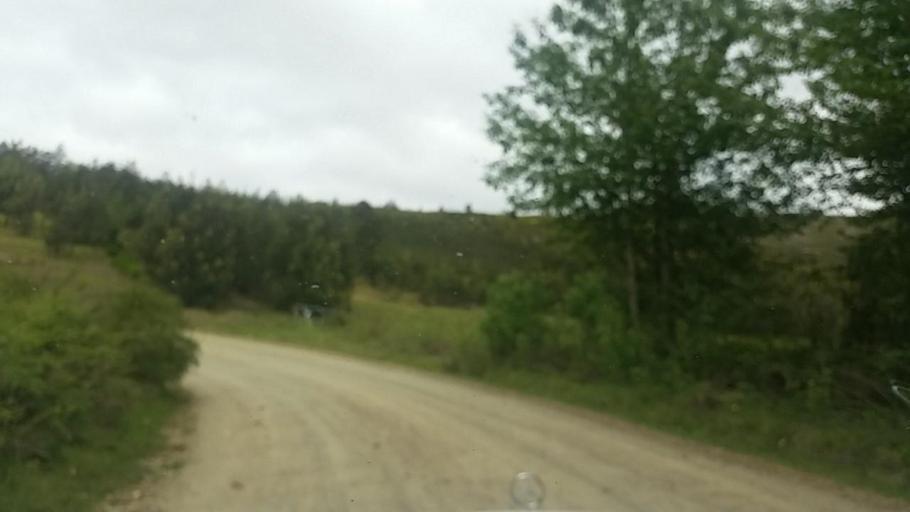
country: ZA
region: Western Cape
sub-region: Eden District Municipality
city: Knysna
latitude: -33.7474
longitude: 23.1690
